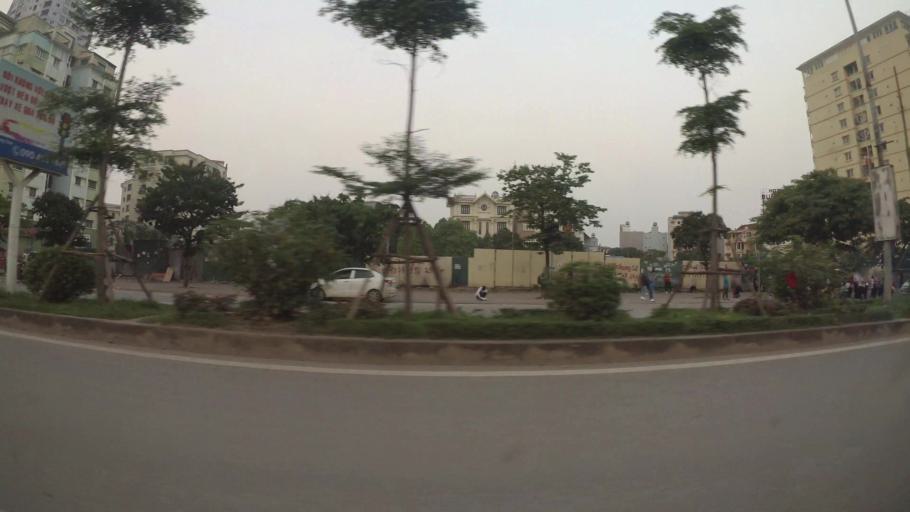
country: VN
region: Ha Noi
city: Tay Ho
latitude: 21.0672
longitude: 105.7873
